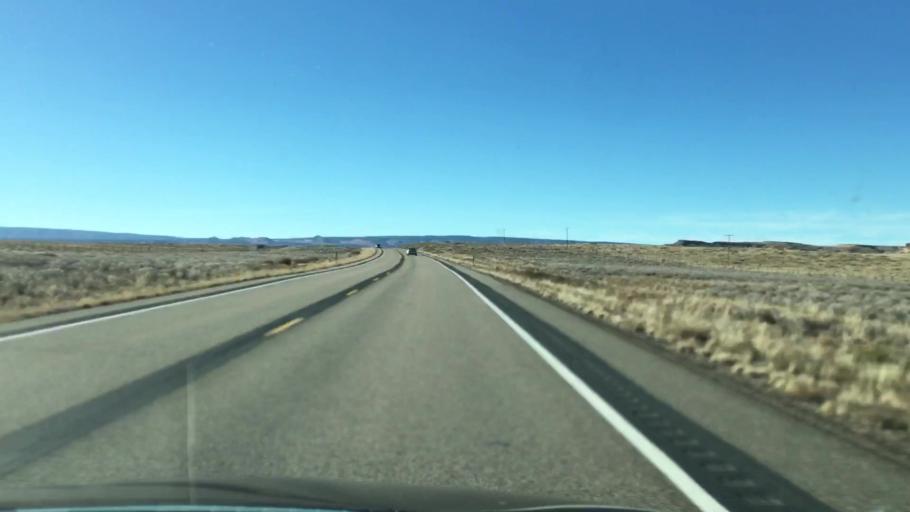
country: US
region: Arizona
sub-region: Coconino County
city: Page
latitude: 37.1053
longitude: -111.8390
